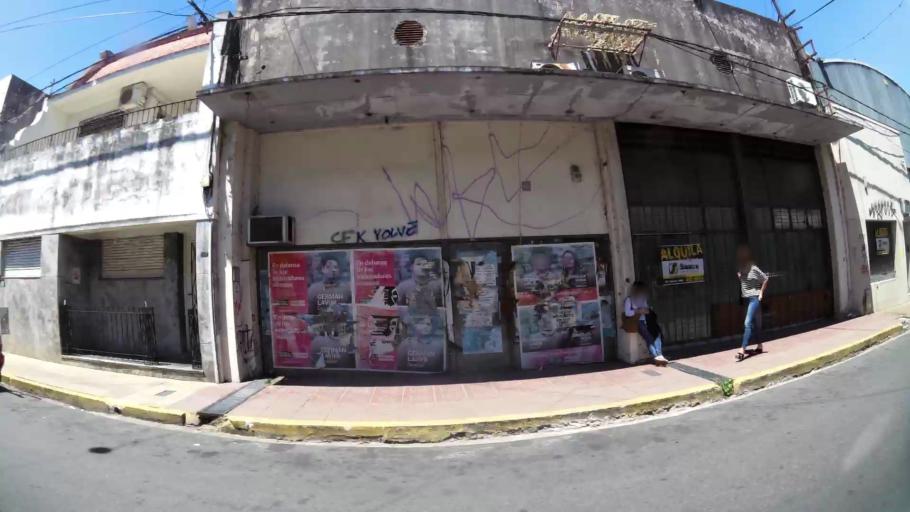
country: AR
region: Santa Fe
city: Santa Fe de la Vera Cruz
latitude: -31.6445
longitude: -60.7087
